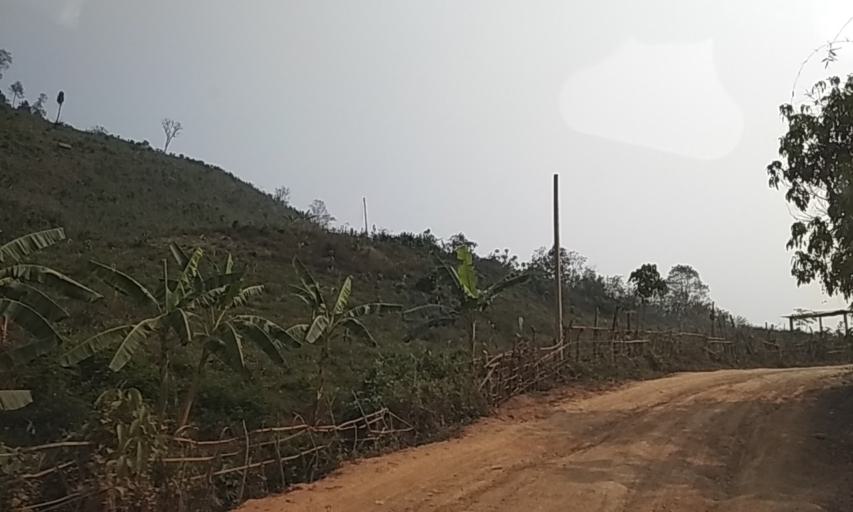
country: TH
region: Nan
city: Chaloem Phra Kiat
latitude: 19.9255
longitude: 101.1609
